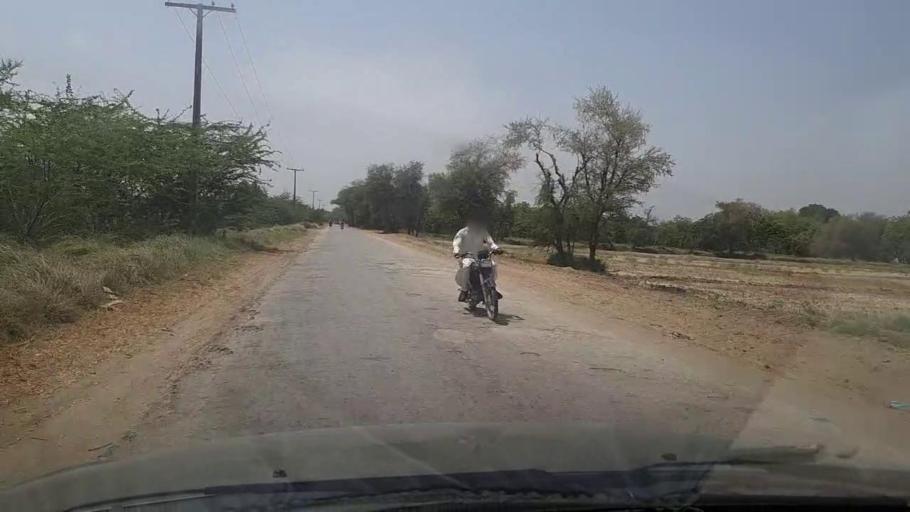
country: PK
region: Sindh
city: Bhiria
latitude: 26.8983
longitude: 68.2227
